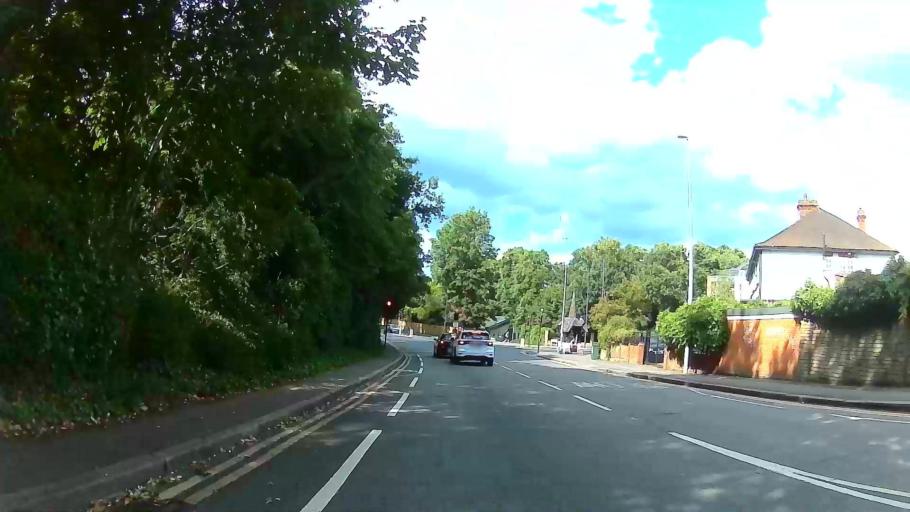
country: GB
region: England
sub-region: Greater London
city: Woodford Green
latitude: 51.5814
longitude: 0.0200
